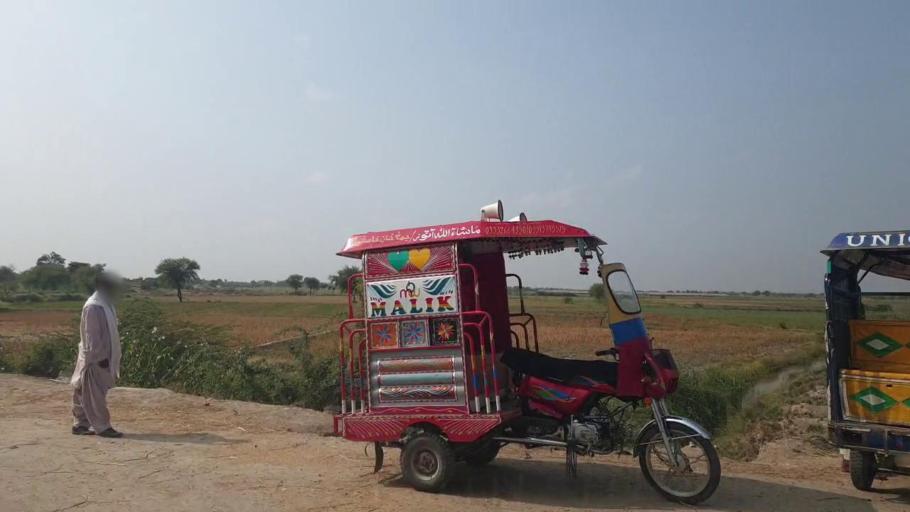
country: PK
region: Sindh
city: Talhar
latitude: 24.7761
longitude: 68.7746
